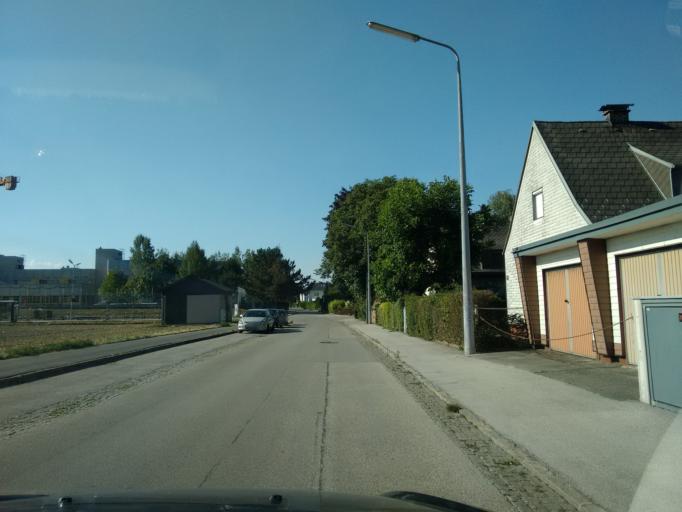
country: AT
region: Upper Austria
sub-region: Politischer Bezirk Linz-Land
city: Traun
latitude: 48.2268
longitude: 14.2485
